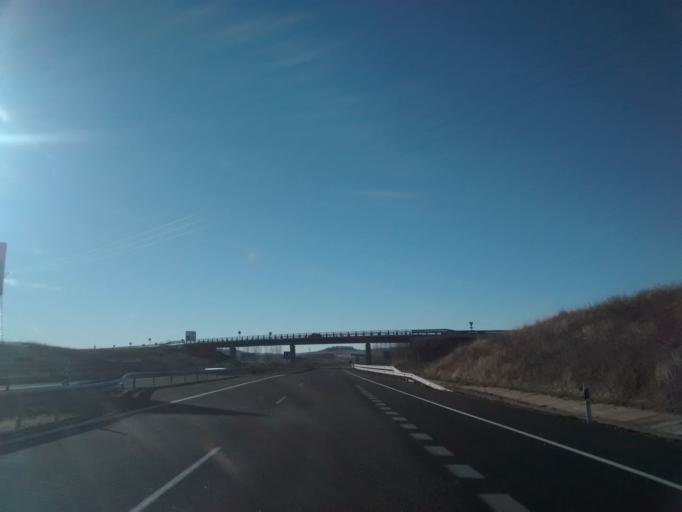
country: ES
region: Castille and Leon
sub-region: Provincia de Palencia
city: Herrera de Pisuerga
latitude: 42.6094
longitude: -4.3490
